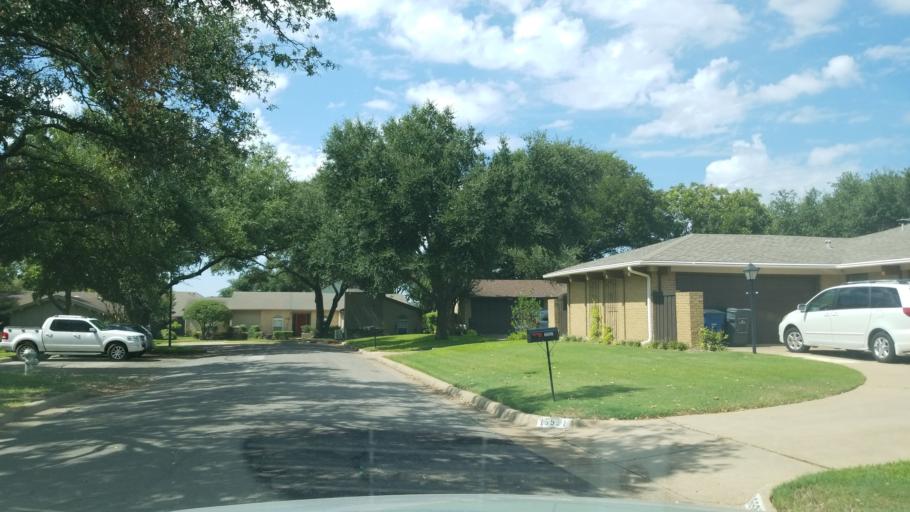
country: US
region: Texas
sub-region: Dallas County
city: Addison
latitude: 32.9605
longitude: -96.7838
